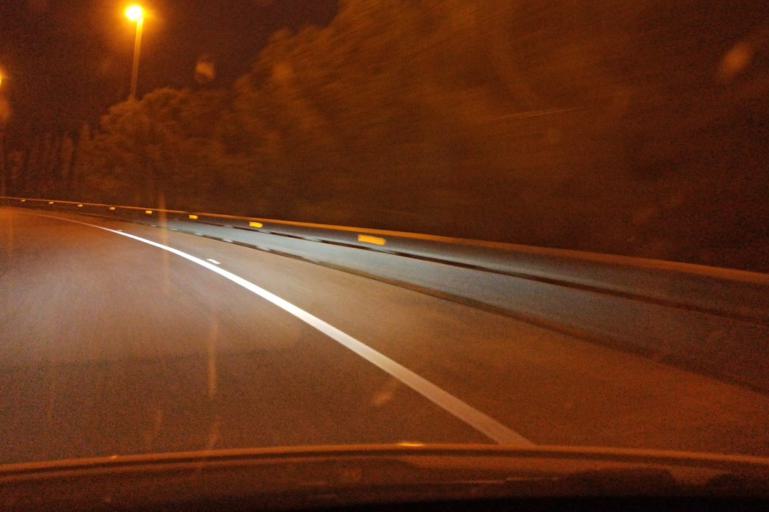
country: ES
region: Catalonia
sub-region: Provincia de Tarragona
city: Cunit
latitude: 41.2070
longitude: 1.6522
